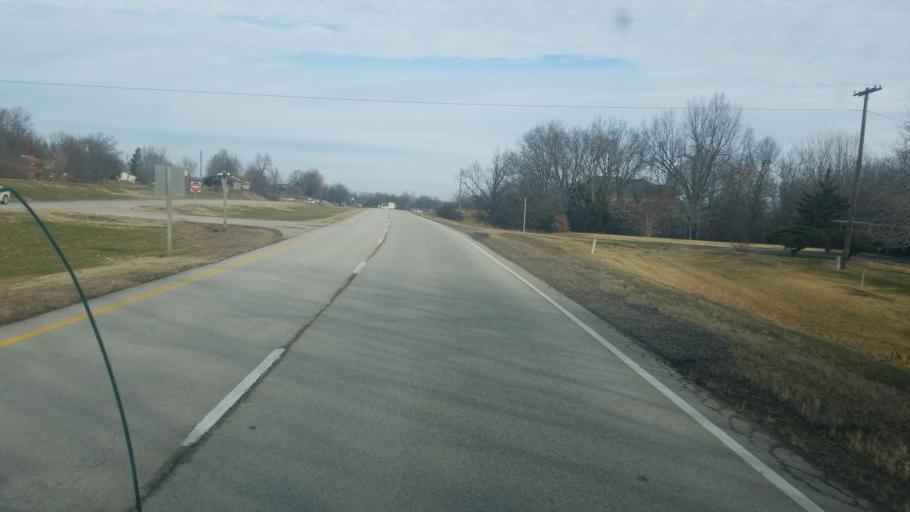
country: US
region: Missouri
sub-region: Stoddard County
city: Bloomfield
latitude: 36.8682
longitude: -89.9296
